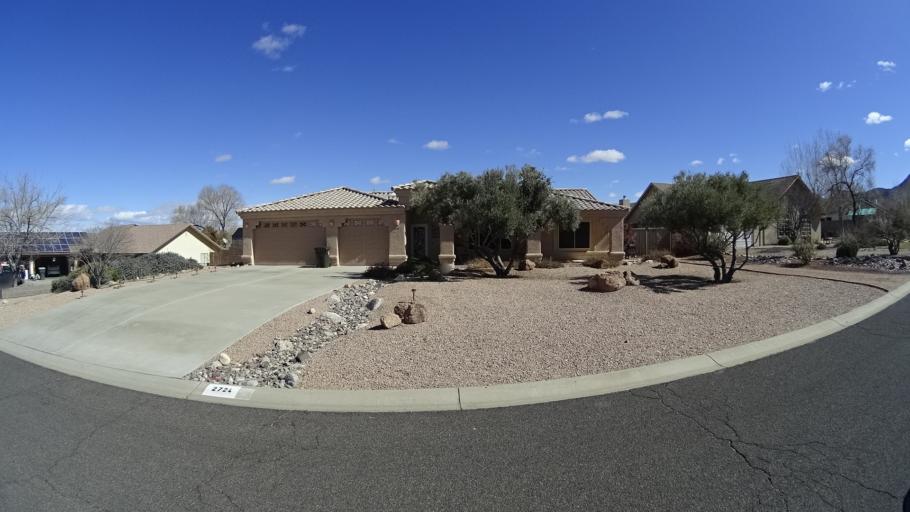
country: US
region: Arizona
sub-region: Mohave County
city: Kingman
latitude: 35.2019
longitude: -113.9664
